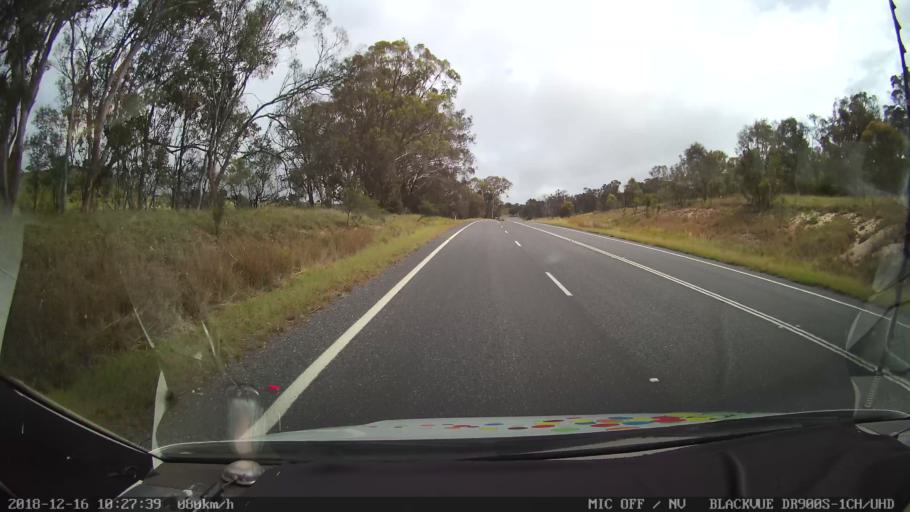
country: AU
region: New South Wales
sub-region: Tenterfield Municipality
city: Carrolls Creek
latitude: -29.1309
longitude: 151.9958
